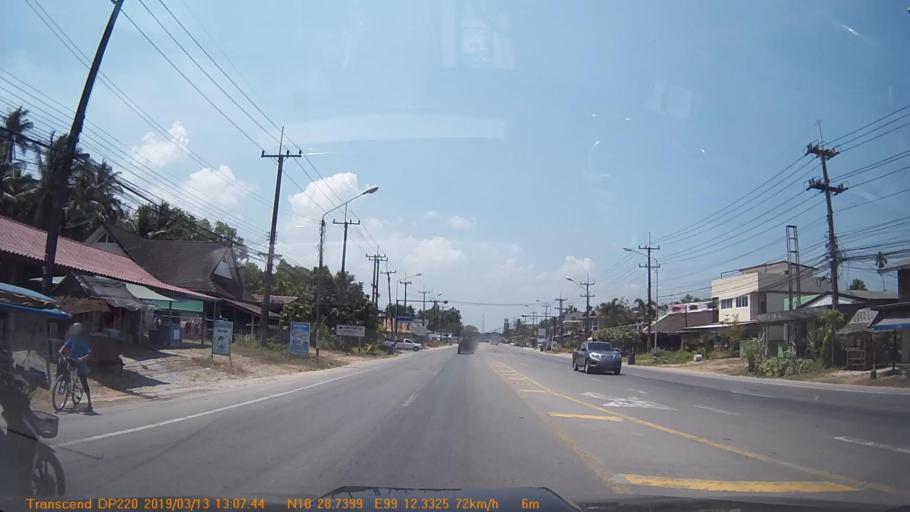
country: TH
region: Chumphon
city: Chumphon
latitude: 10.4791
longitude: 99.2054
